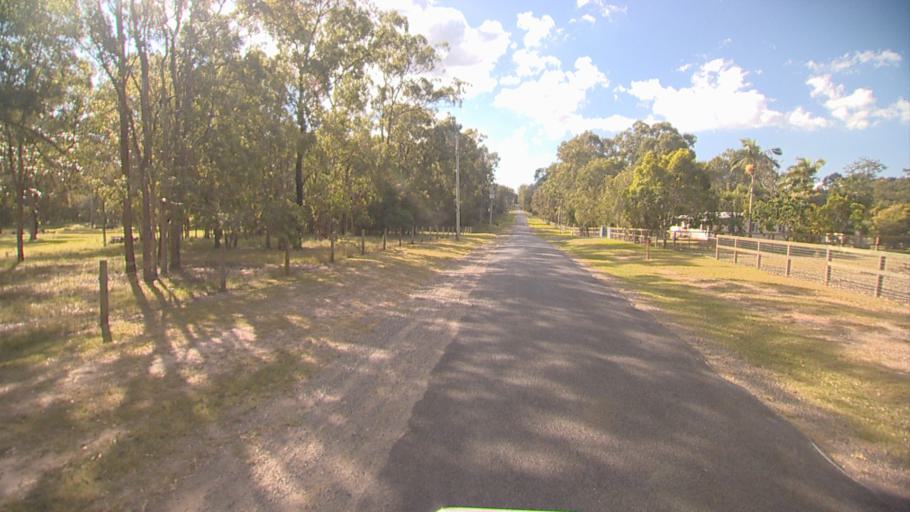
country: AU
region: Queensland
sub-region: Gold Coast
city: Yatala
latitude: -27.6651
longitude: 153.2407
